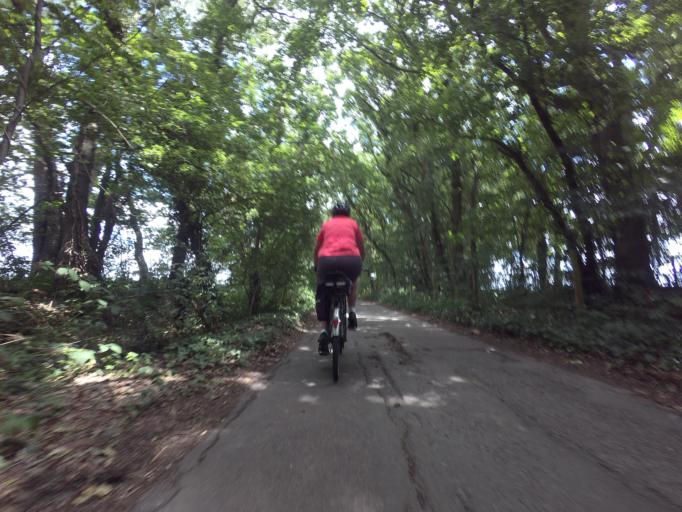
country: GB
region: England
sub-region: East Sussex
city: Hailsham
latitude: 50.8352
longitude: 0.2088
